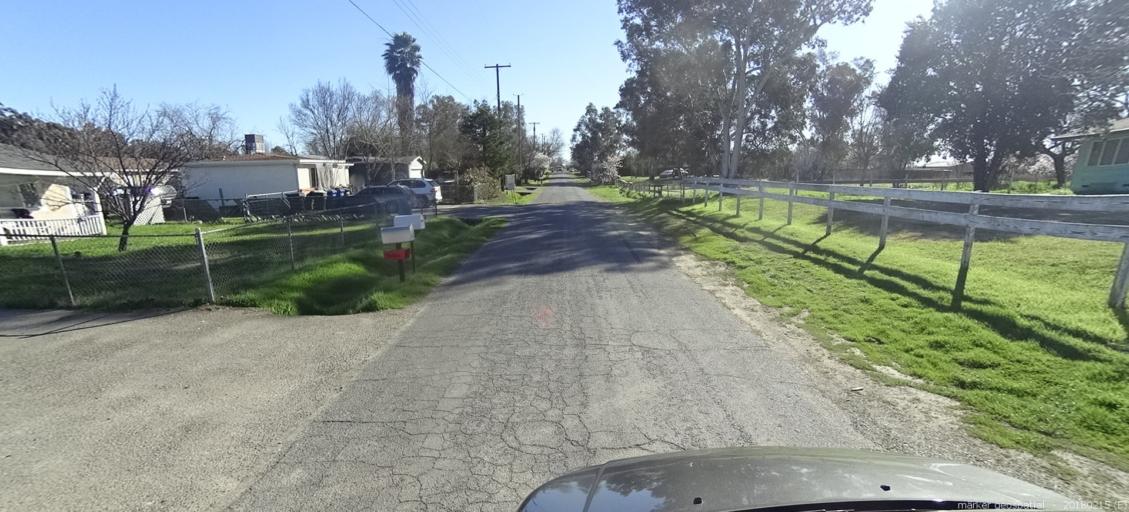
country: US
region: California
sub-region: Sacramento County
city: Rio Linda
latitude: 38.6738
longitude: -121.4615
